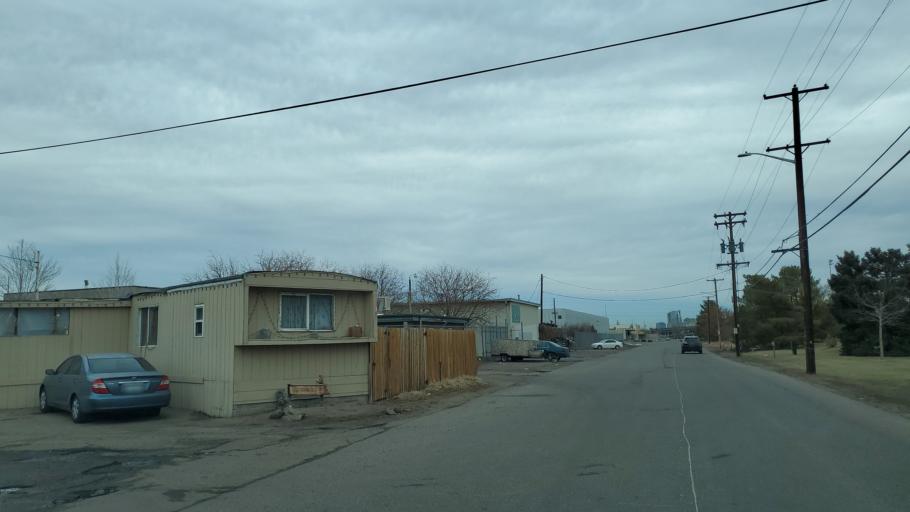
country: US
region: Colorado
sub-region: Denver County
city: Denver
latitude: 39.6992
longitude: -104.9968
